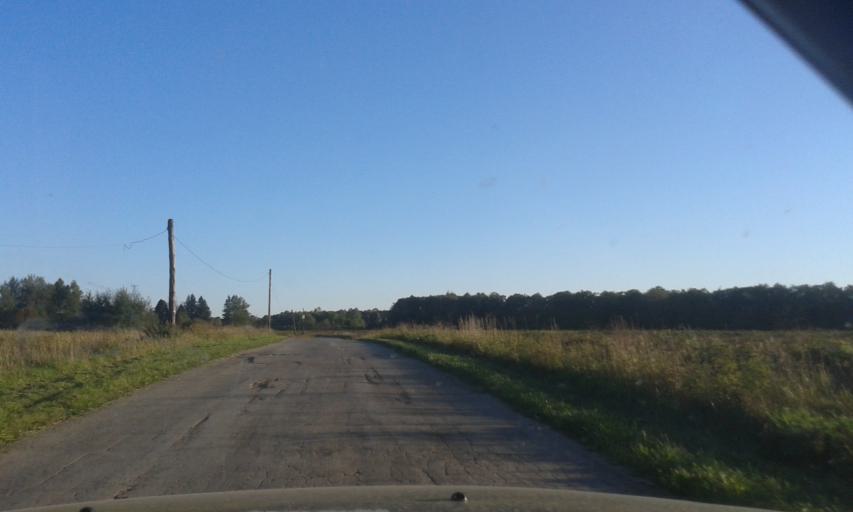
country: RU
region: Tula
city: Krapivna
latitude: 54.1181
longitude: 37.1524
